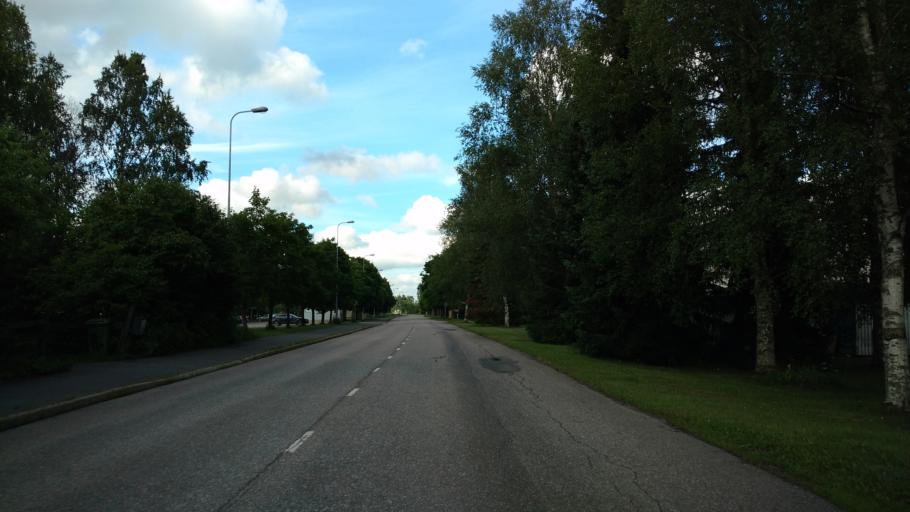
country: FI
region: Varsinais-Suomi
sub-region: Salo
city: Salo
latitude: 60.3982
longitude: 23.1453
